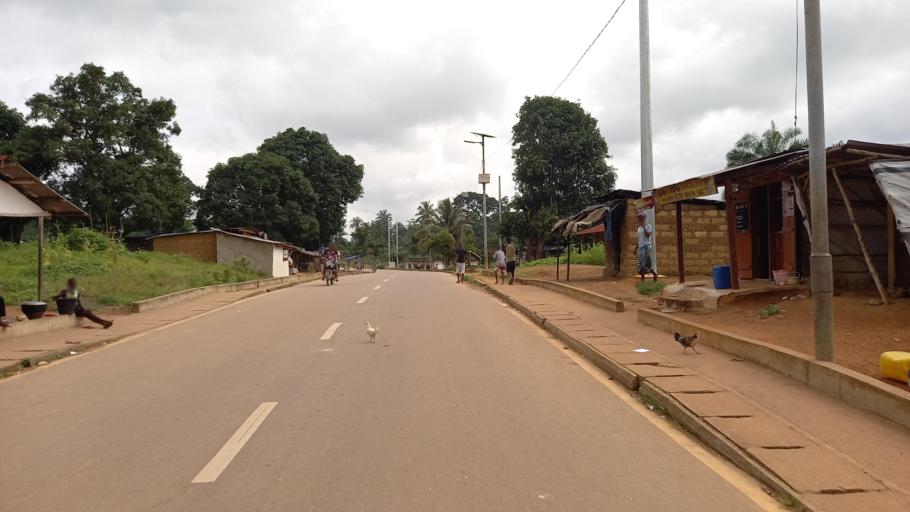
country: SL
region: Eastern Province
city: Kailahun
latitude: 8.2831
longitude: -10.5734
